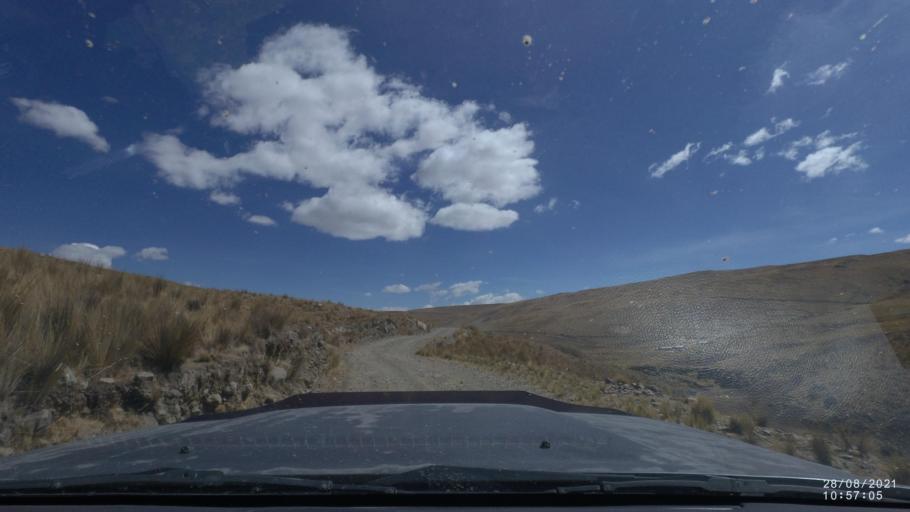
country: BO
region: Cochabamba
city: Cochabamba
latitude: -17.1897
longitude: -66.2502
